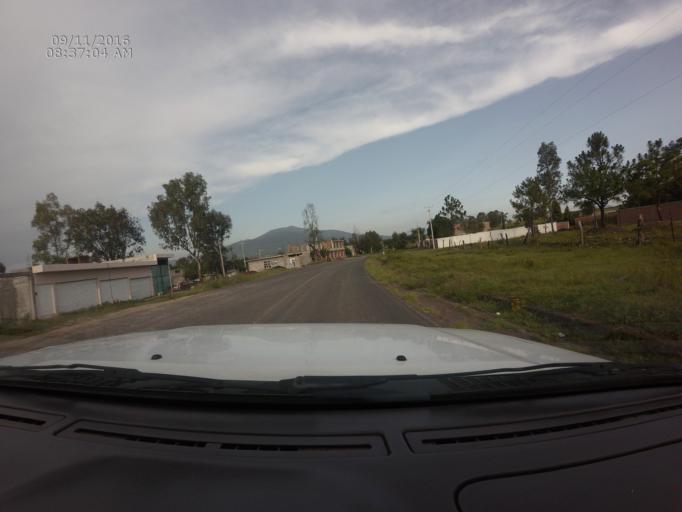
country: MX
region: Michoacan
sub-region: Morelia
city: La Mintzita (Piedra Dura)
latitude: 19.6226
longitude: -101.2717
